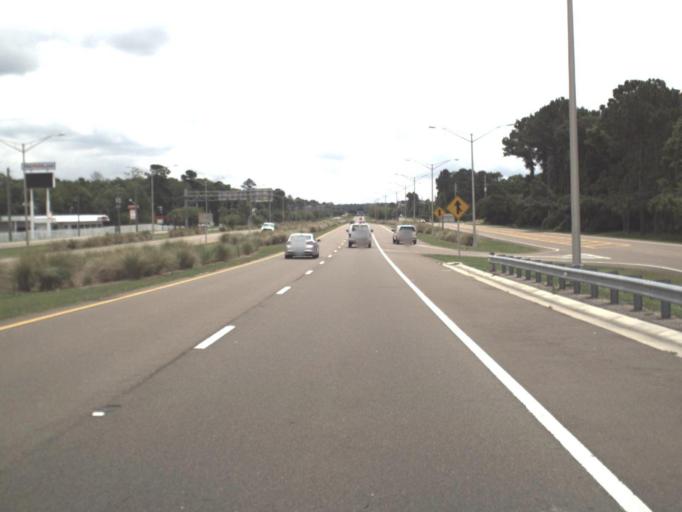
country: US
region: Florida
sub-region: Nassau County
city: Nassau Village-Ratliff
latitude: 30.4842
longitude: -81.6614
